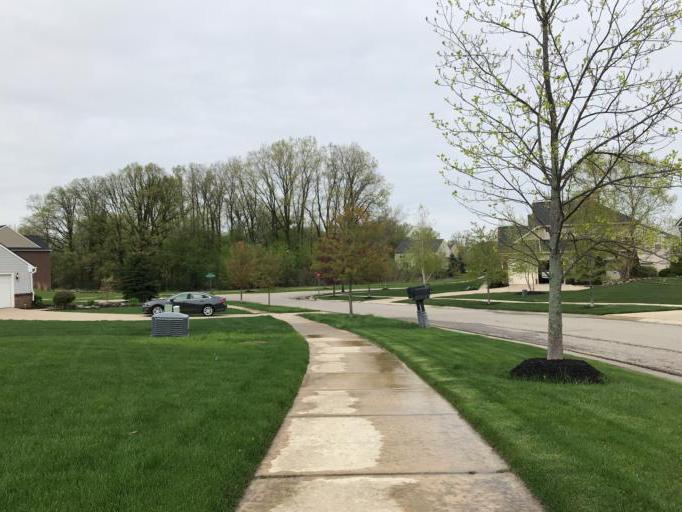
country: US
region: Michigan
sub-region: Oakland County
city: South Lyon
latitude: 42.4792
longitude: -83.6250
